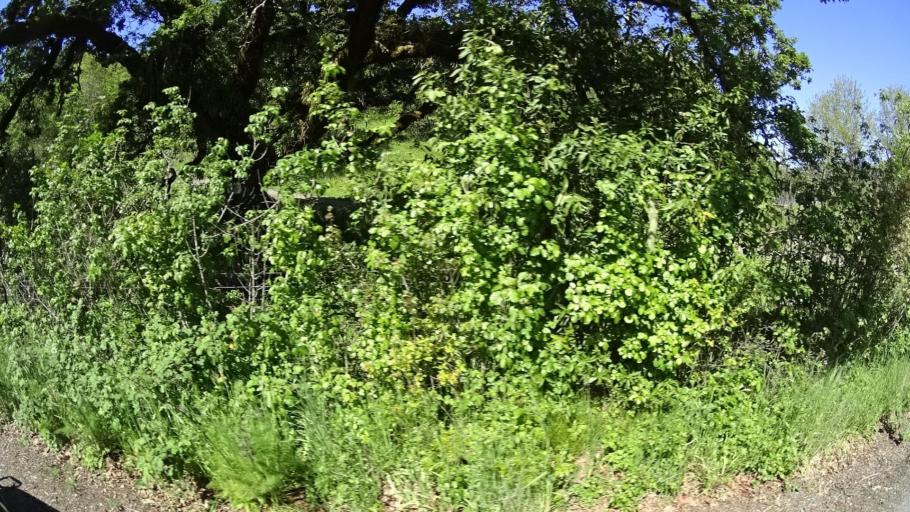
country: US
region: California
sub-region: Humboldt County
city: Rio Dell
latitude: 40.2323
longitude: -124.1165
